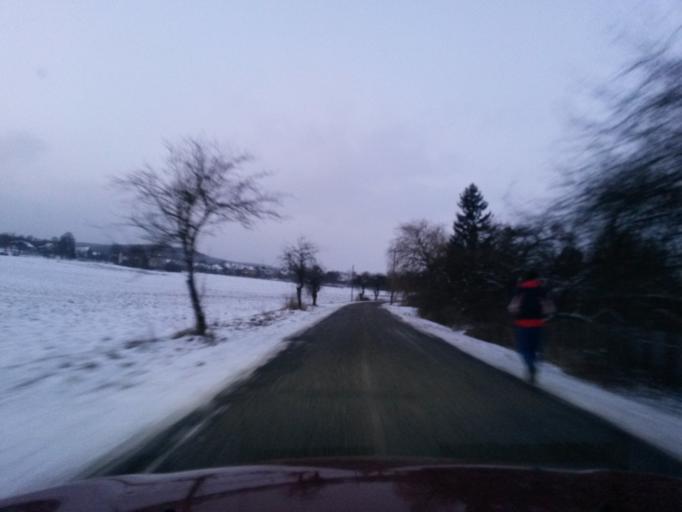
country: SK
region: Kosicky
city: Kosice
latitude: 48.7417
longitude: 21.3236
